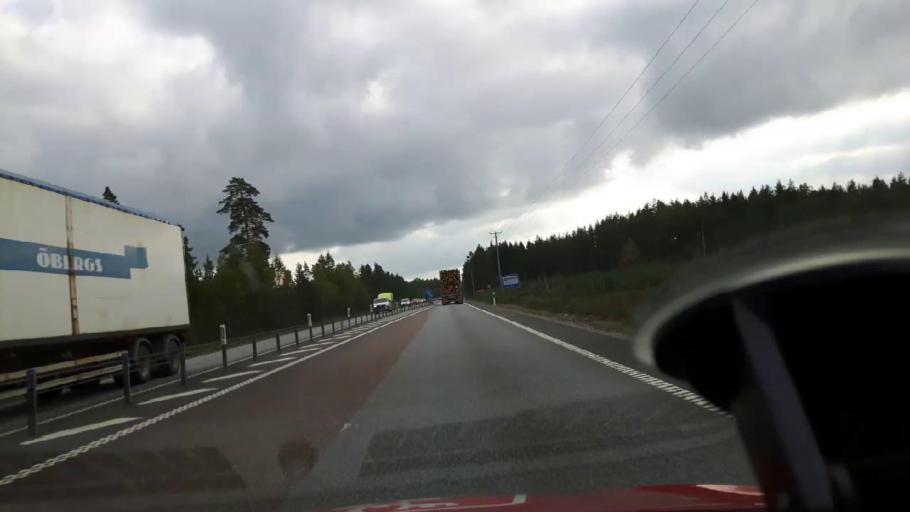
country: SE
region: Gaevleborg
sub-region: Gavle Kommun
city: Norrsundet
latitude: 61.0363
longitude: 16.9686
